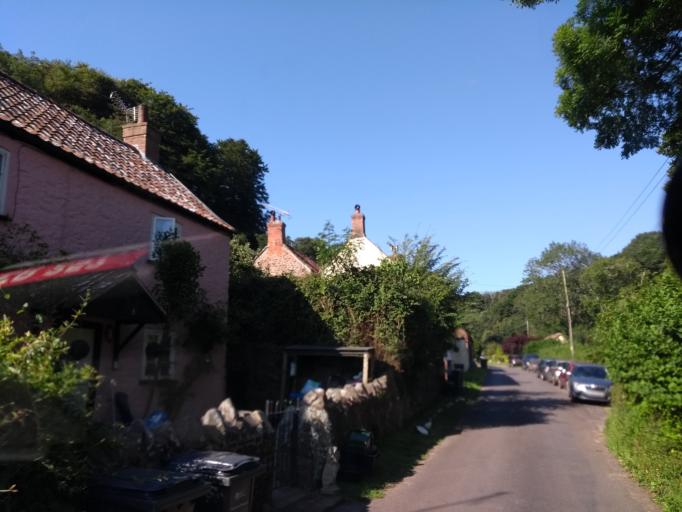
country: GB
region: England
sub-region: Somerset
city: Bishops Lydeard
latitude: 51.1606
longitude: -3.2116
